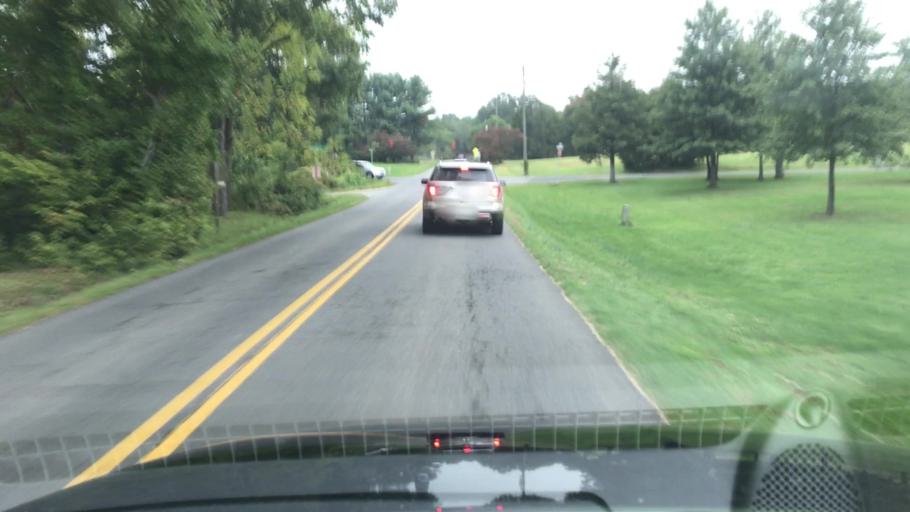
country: US
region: Virginia
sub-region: Fauquier County
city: New Baltimore
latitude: 38.7277
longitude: -77.6609
